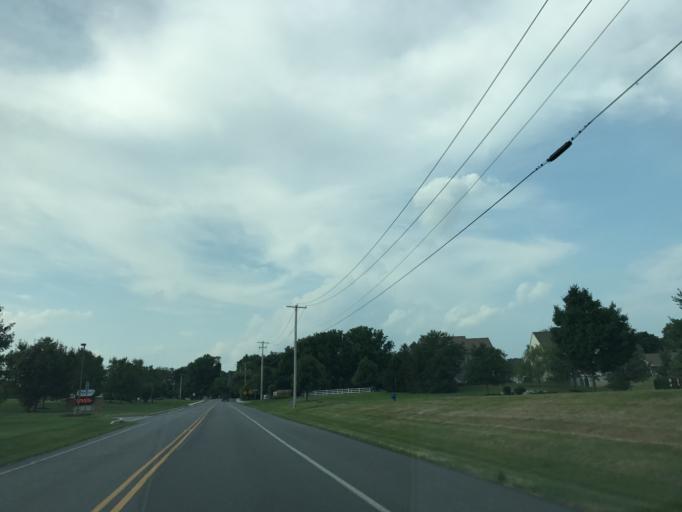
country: US
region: Pennsylvania
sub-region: Lancaster County
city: Mount Joy
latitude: 40.1119
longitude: -76.5322
